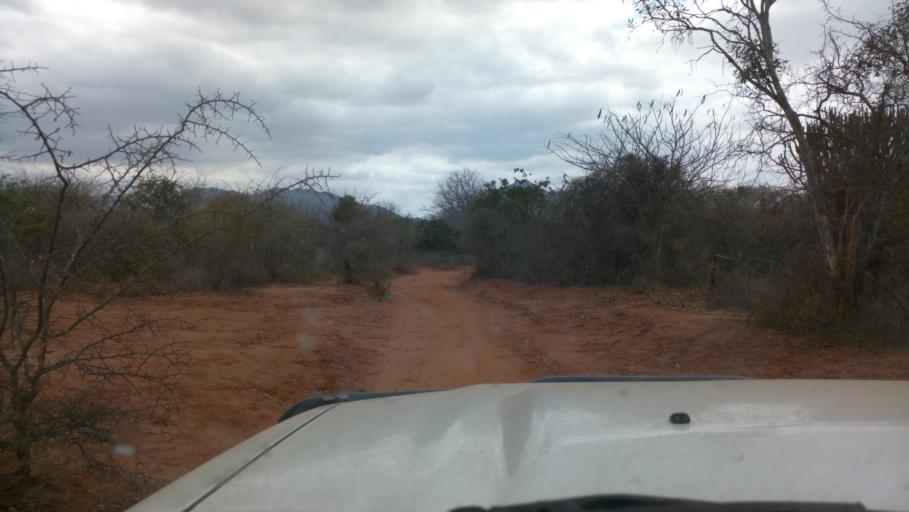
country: KE
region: Kitui
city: Kitui
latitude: -1.8634
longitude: 38.3667
